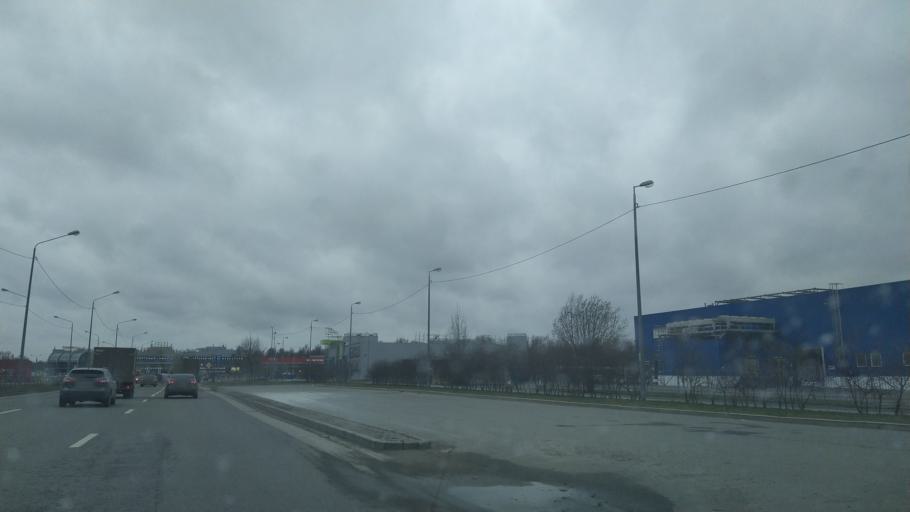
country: RU
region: St.-Petersburg
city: Komendantsky aerodrom
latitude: 60.0021
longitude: 30.2707
